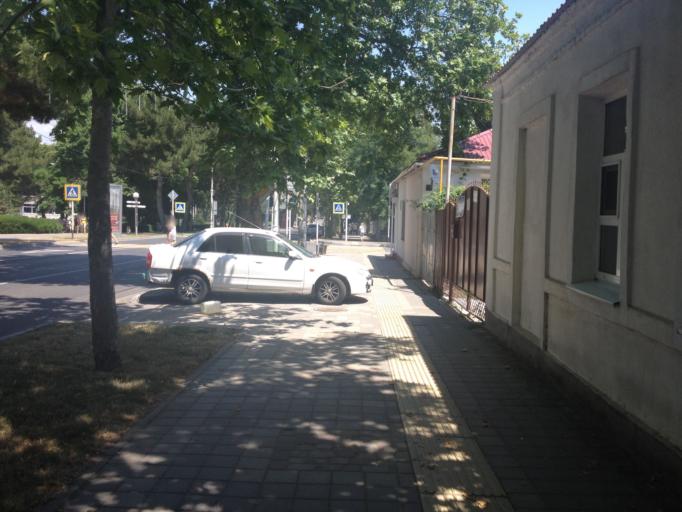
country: RU
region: Krasnodarskiy
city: Anapa
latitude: 44.8933
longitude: 37.3155
